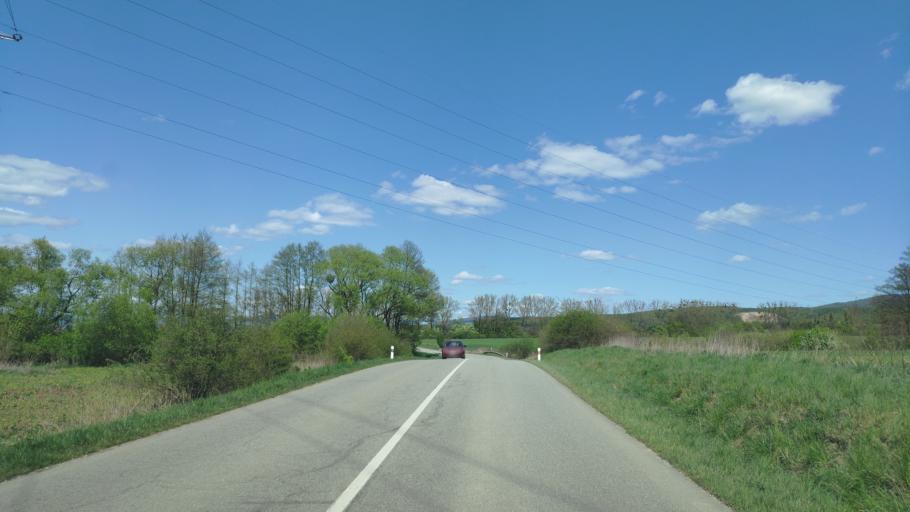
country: SK
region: Kosicky
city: Kosice
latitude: 48.6745
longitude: 21.4188
